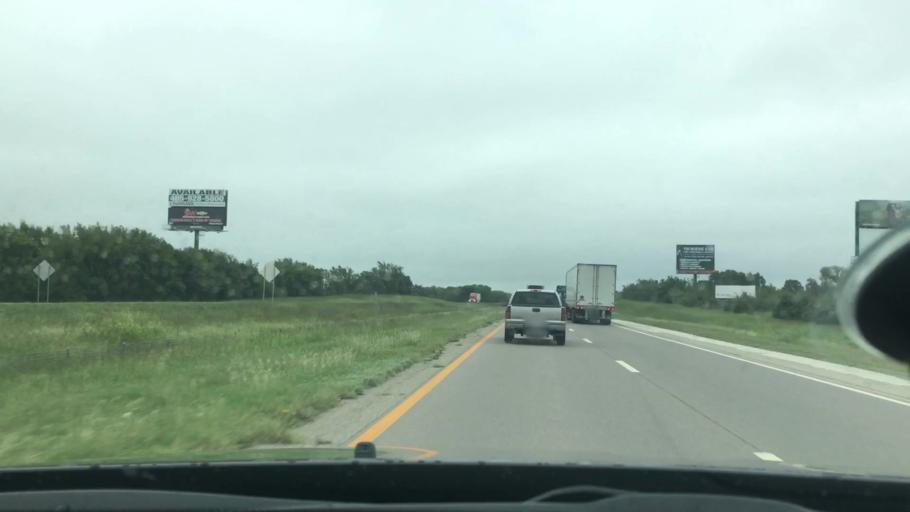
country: US
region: Oklahoma
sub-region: Okfuskee County
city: Okemah
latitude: 35.4284
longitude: -96.2447
